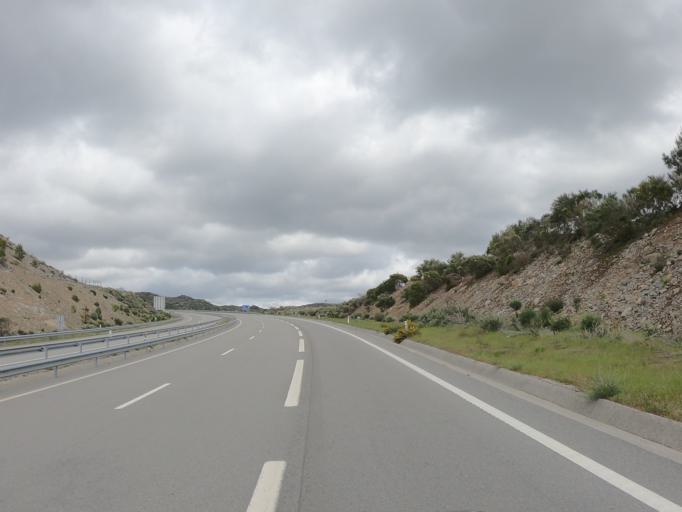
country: PT
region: Vila Real
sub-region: Vila Real
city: Vila Real
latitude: 41.3651
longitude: -7.6865
